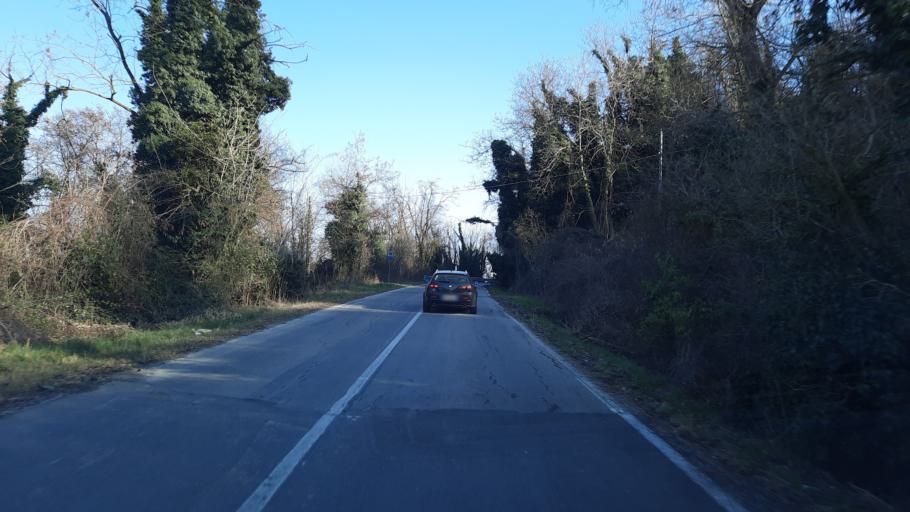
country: IT
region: Piedmont
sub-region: Provincia di Alessandria
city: Camino
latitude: 45.1659
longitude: 8.2898
